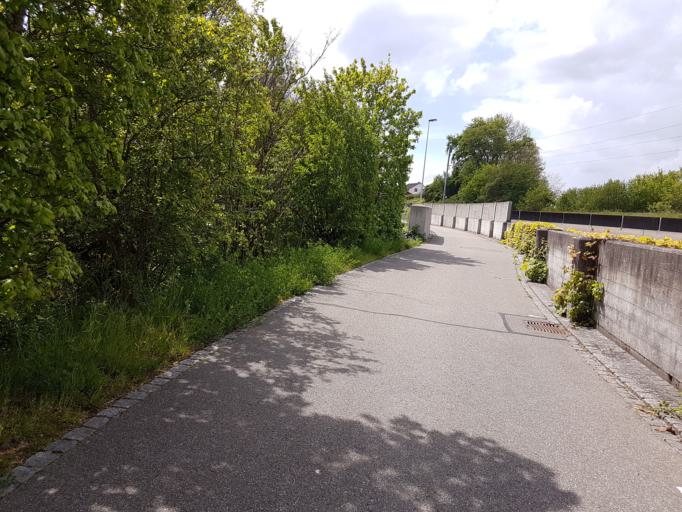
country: CH
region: Aargau
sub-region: Bezirk Zurzach
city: Klingnau
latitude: 47.5681
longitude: 8.2572
